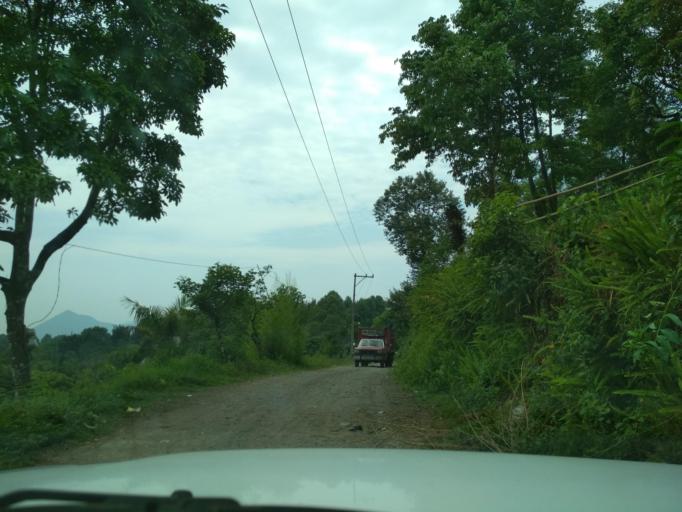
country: MX
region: Veracruz
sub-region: La Perla
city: La Perla
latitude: 18.9217
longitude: -97.1274
